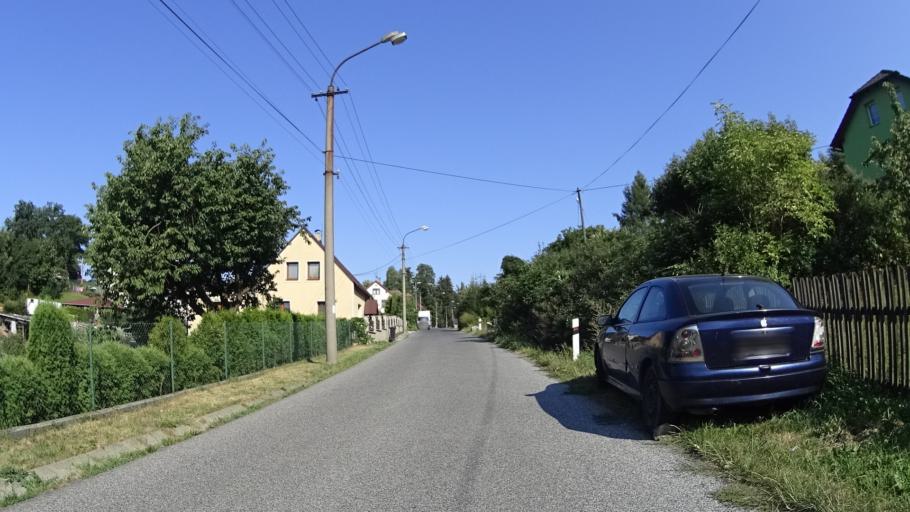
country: CZ
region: Liberecky
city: Hodkovice nad Mohelkou
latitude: 50.6995
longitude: 15.0954
